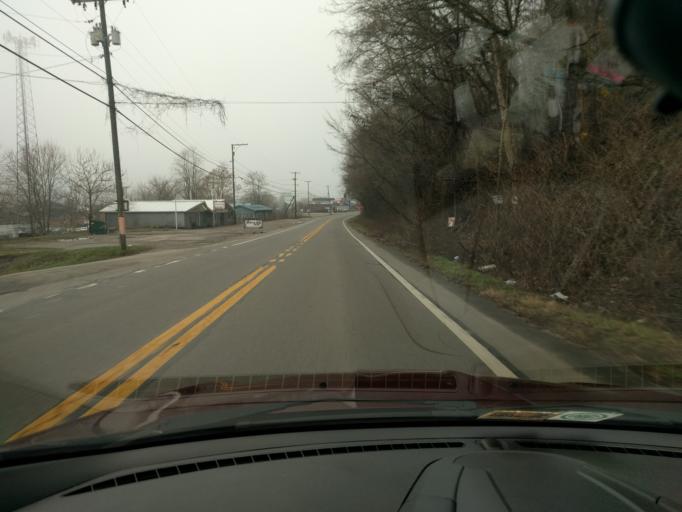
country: US
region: West Virginia
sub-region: Kanawha County
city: Chesapeake
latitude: 38.2084
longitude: -81.4684
